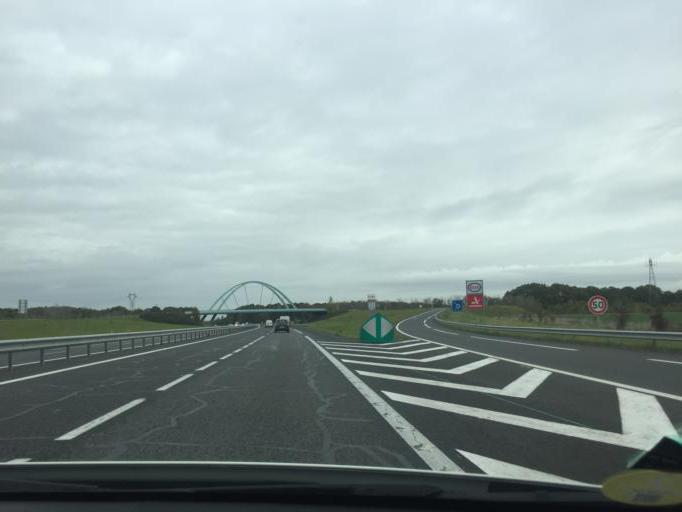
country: FR
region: Bourgogne
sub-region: Departement de l'Yonne
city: Egriselles-le-Bocage
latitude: 48.1636
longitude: 3.1761
